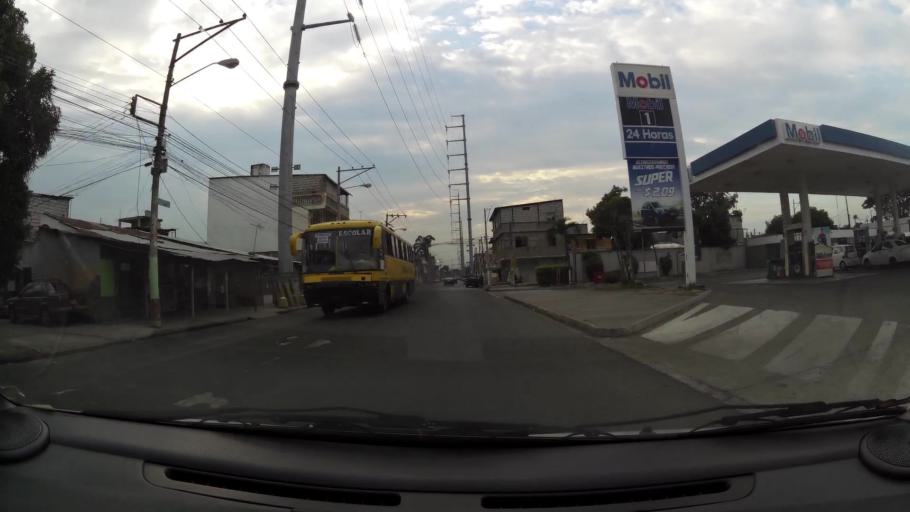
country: EC
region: Guayas
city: Guayaquil
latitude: -2.2494
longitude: -79.8794
